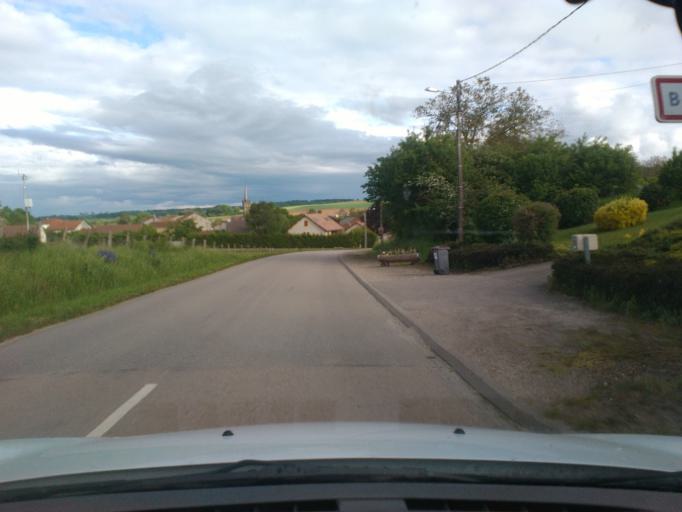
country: FR
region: Lorraine
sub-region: Departement des Vosges
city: Mirecourt
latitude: 48.3155
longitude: 6.0505
